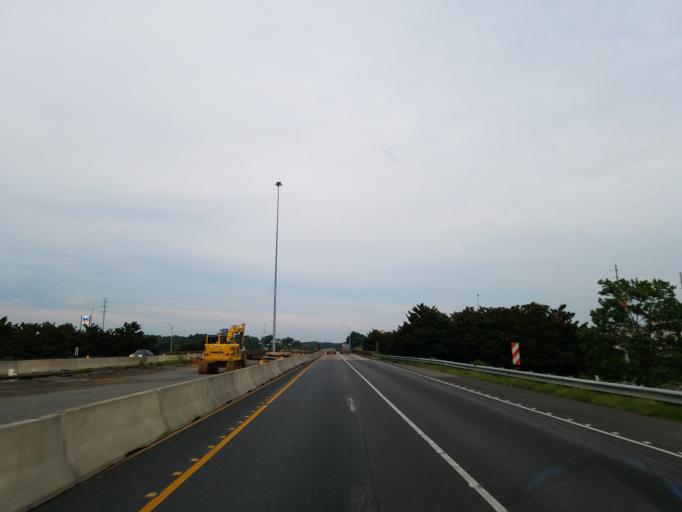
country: US
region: Alabama
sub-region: Tuscaloosa County
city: Tuscaloosa
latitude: 33.1714
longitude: -87.5267
